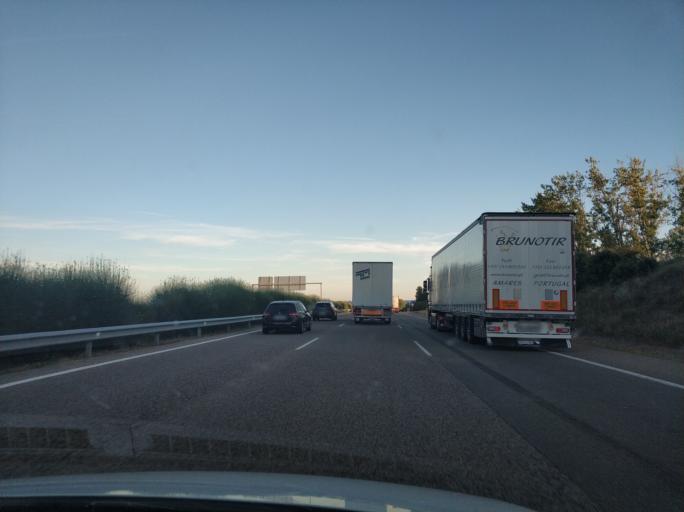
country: ES
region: Castille and Leon
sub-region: Provincia de Zamora
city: Benavente
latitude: 42.0343
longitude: -5.6721
